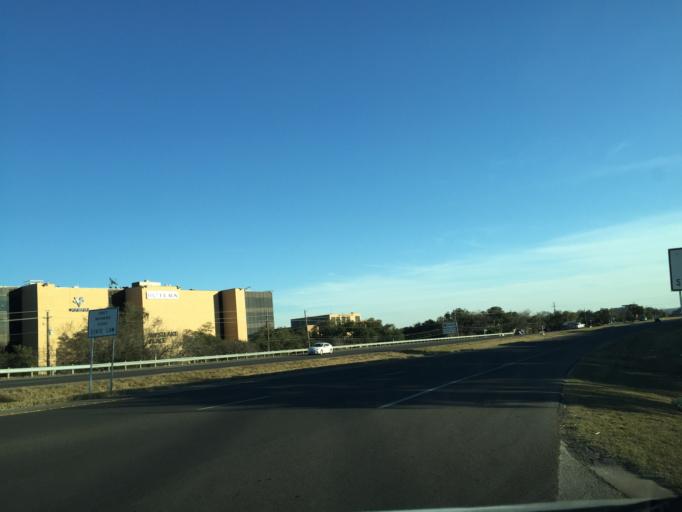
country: US
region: Texas
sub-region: Travis County
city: Rollingwood
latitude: 30.2741
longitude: -97.8179
